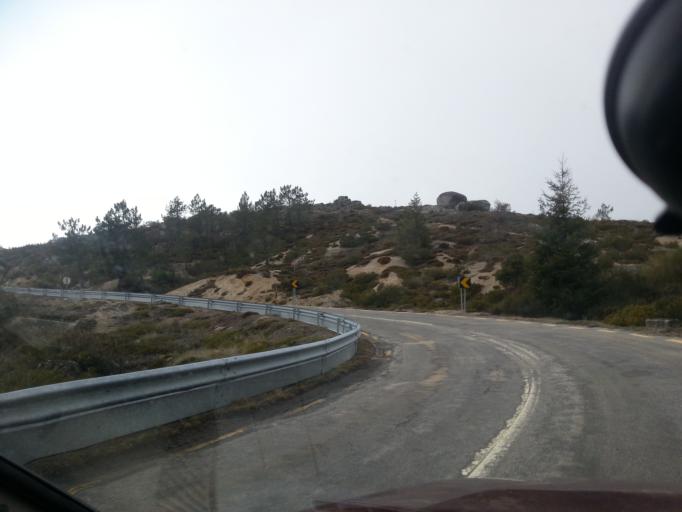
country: PT
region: Guarda
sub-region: Manteigas
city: Manteigas
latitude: 40.4165
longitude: -7.5540
